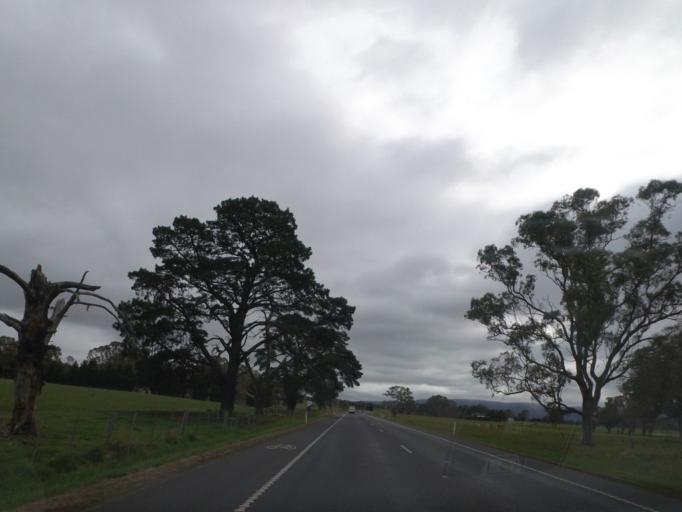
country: AU
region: Victoria
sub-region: Whittlesea
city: Whittlesea
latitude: -37.5537
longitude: 145.1093
